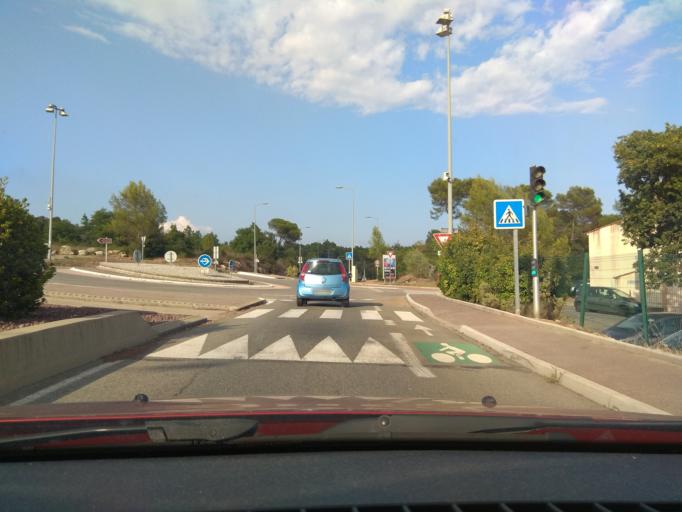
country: FR
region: Provence-Alpes-Cote d'Azur
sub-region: Departement des Alpes-Maritimes
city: Le Rouret
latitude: 43.6630
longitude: 7.0386
